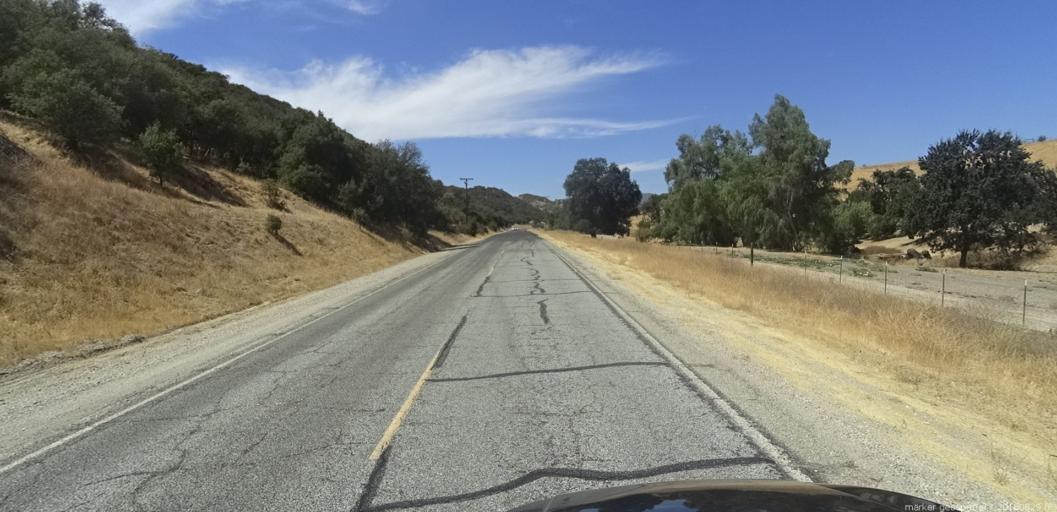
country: US
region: California
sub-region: San Luis Obispo County
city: Lake Nacimiento
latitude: 35.8900
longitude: -120.9275
